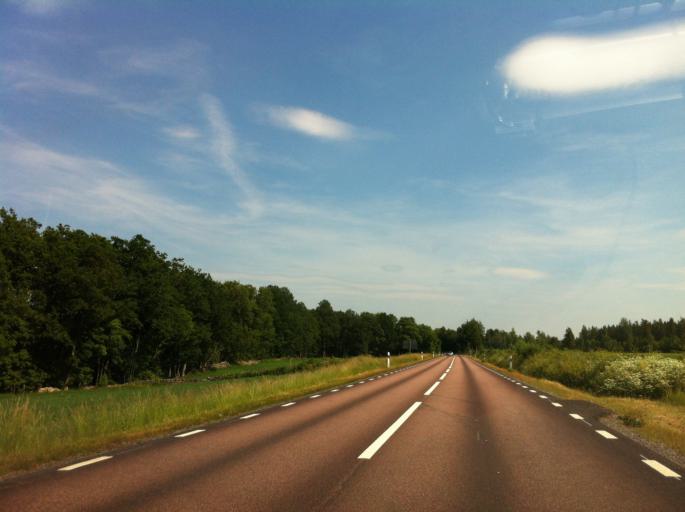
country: SE
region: Kalmar
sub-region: Nybro Kommun
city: Nybro
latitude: 56.7843
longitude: 15.8095
